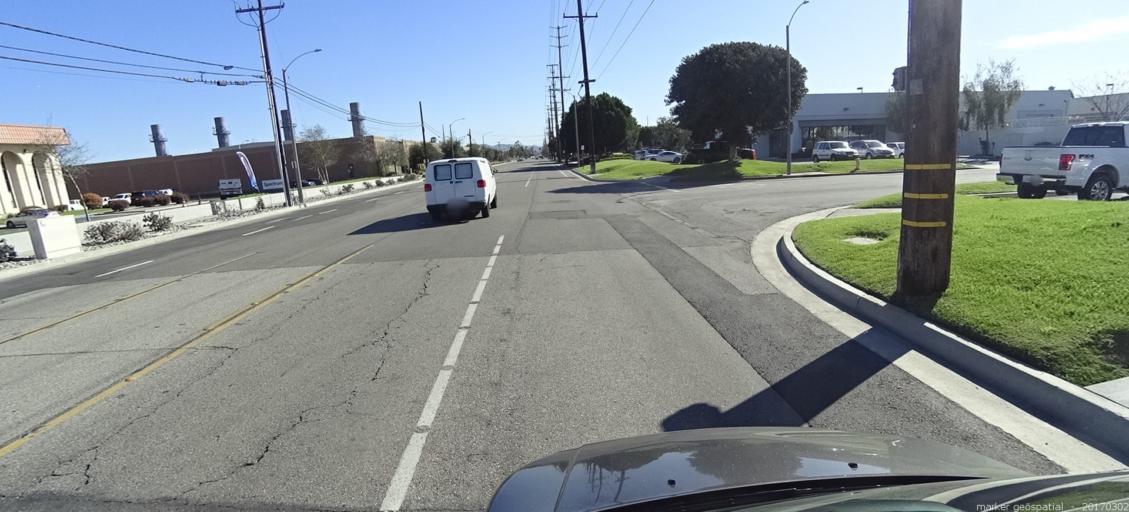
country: US
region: California
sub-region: Orange County
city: Placentia
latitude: 33.8570
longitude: -117.8638
